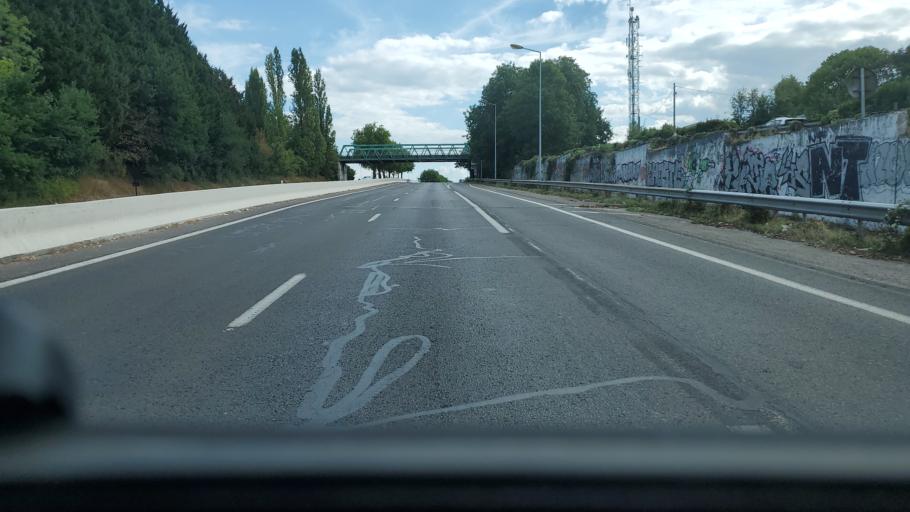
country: FR
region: Ile-de-France
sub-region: Departement de Seine-et-Marne
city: Nanteuil-les-Meaux
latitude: 48.9295
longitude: 2.8803
